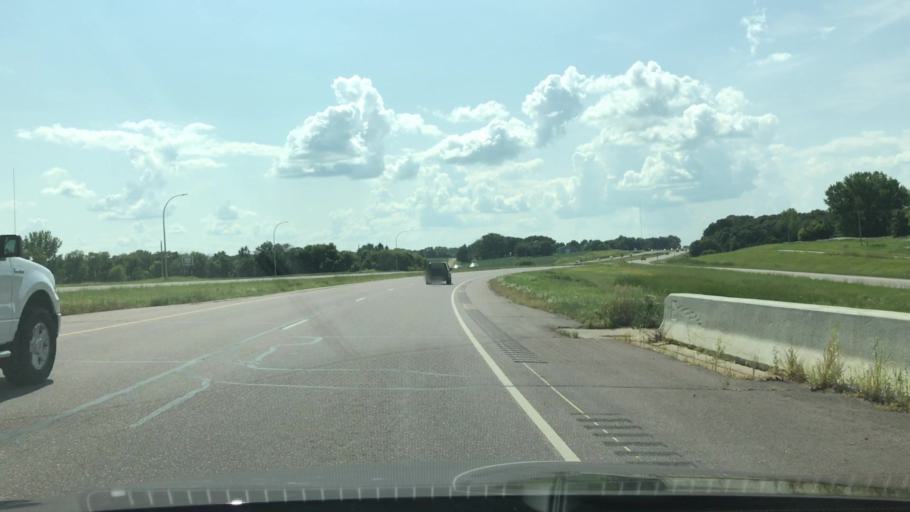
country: US
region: Minnesota
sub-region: Nicollet County
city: North Mankato
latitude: 44.1453
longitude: -94.0850
